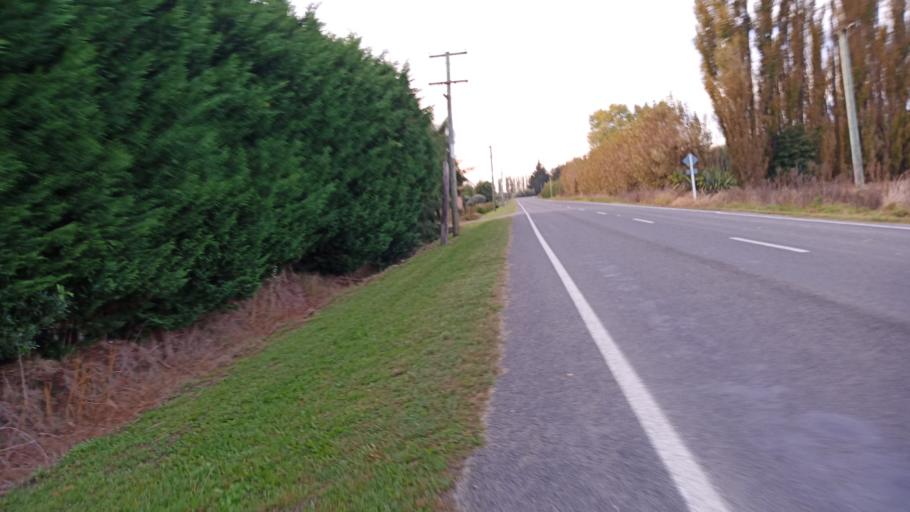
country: NZ
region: Gisborne
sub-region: Gisborne District
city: Gisborne
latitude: -38.6489
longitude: 177.9480
